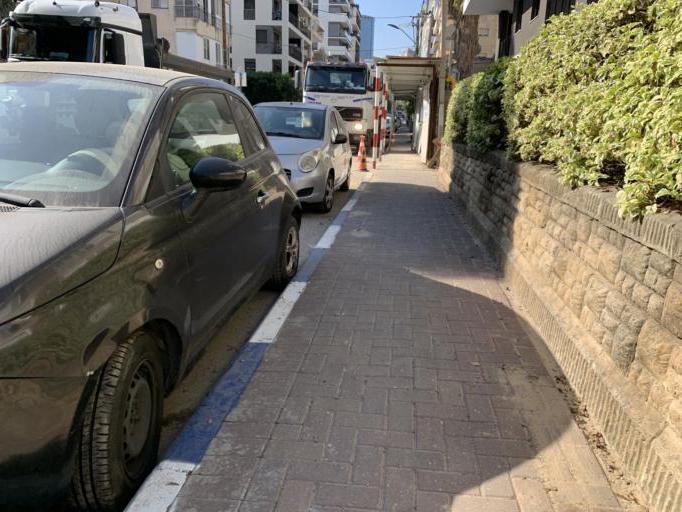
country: IL
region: Tel Aviv
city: Ramat Gan
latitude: 32.0903
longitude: 34.8093
